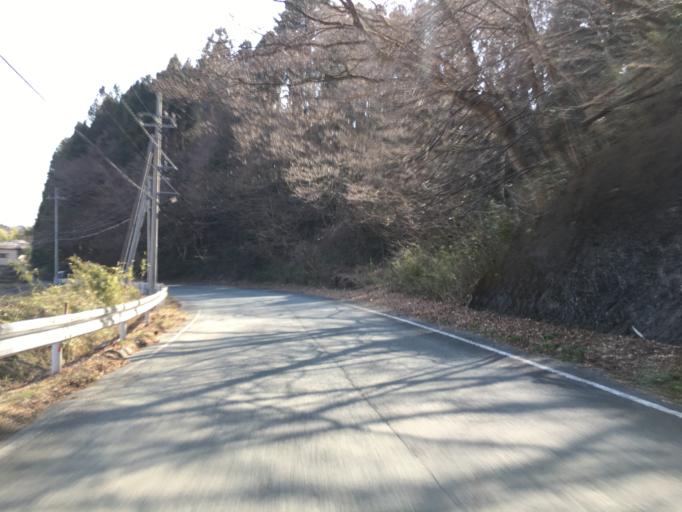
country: JP
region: Ibaraki
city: Takahagi
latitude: 36.8052
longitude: 140.5769
